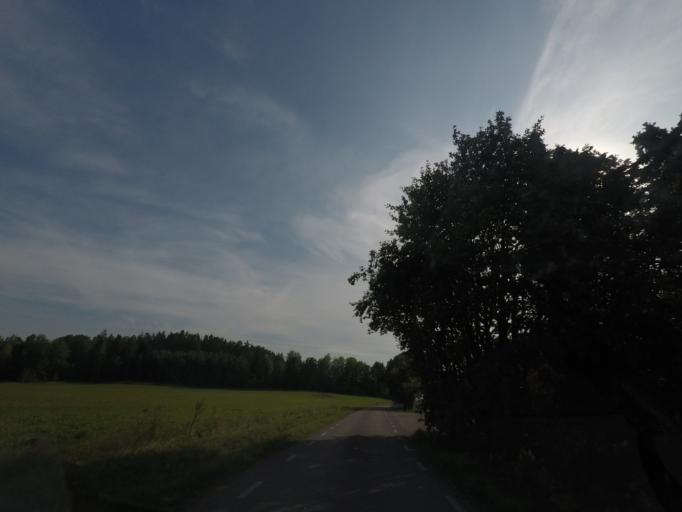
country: SE
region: Vaestmanland
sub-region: Kungsors Kommun
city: Kungsoer
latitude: 59.5015
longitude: 16.1540
